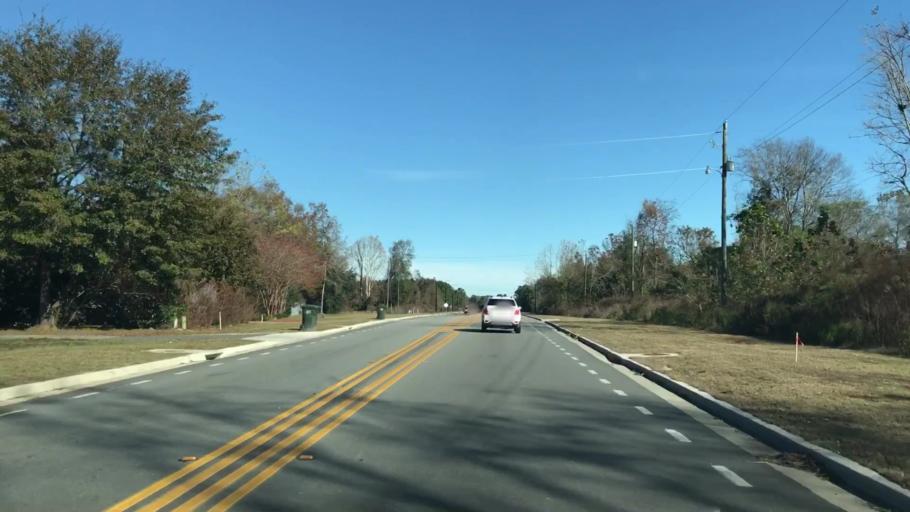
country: US
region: South Carolina
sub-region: Dorchester County
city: Summerville
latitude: 33.0390
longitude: -80.1846
